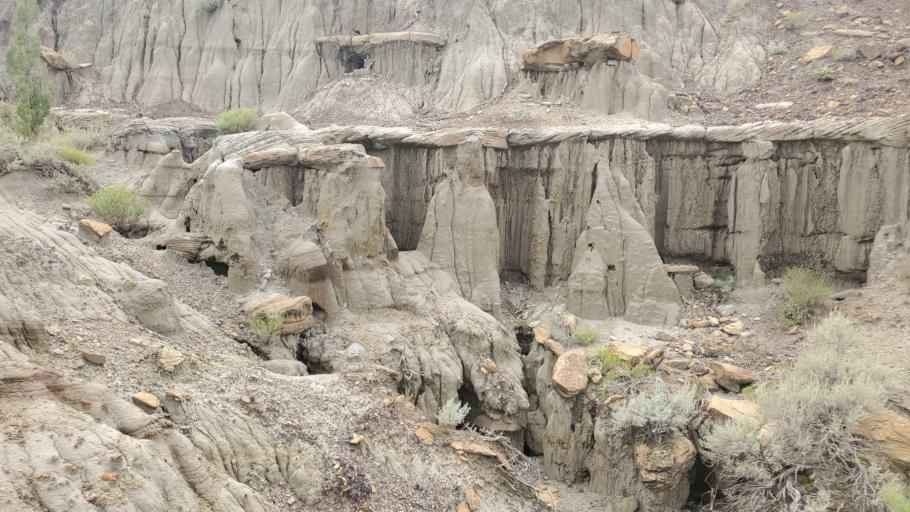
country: US
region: Montana
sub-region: Dawson County
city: Glendive
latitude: 47.0763
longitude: -104.6918
